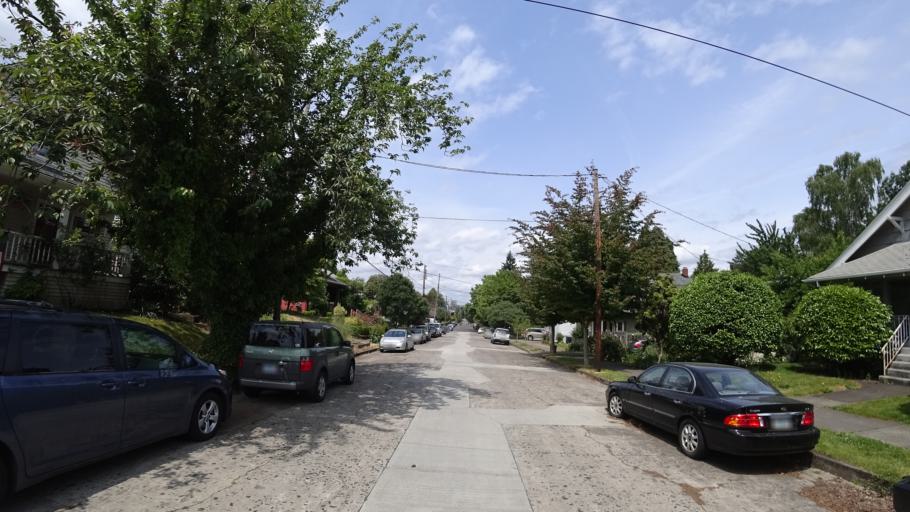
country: US
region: Oregon
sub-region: Multnomah County
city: Portland
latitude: 45.4975
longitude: -122.6558
